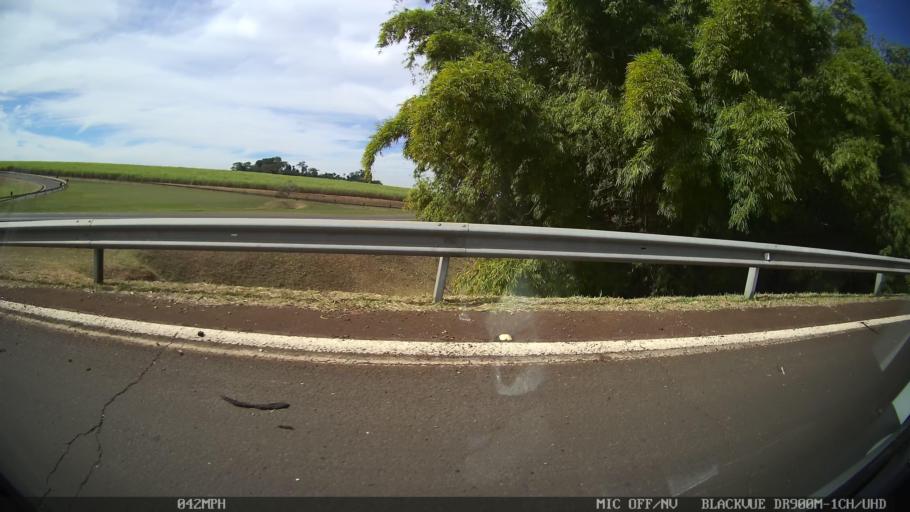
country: BR
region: Sao Paulo
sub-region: Taquaritinga
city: Taquaritinga
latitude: -21.5167
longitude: -48.5403
